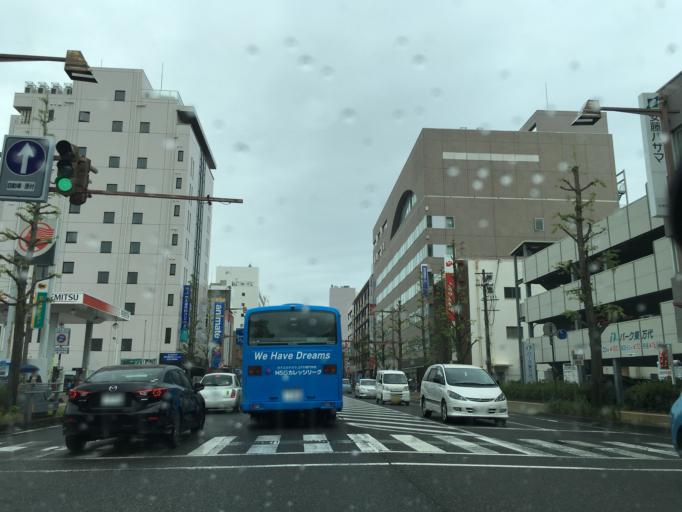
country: JP
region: Niigata
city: Niigata-shi
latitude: 37.9162
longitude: 139.0637
